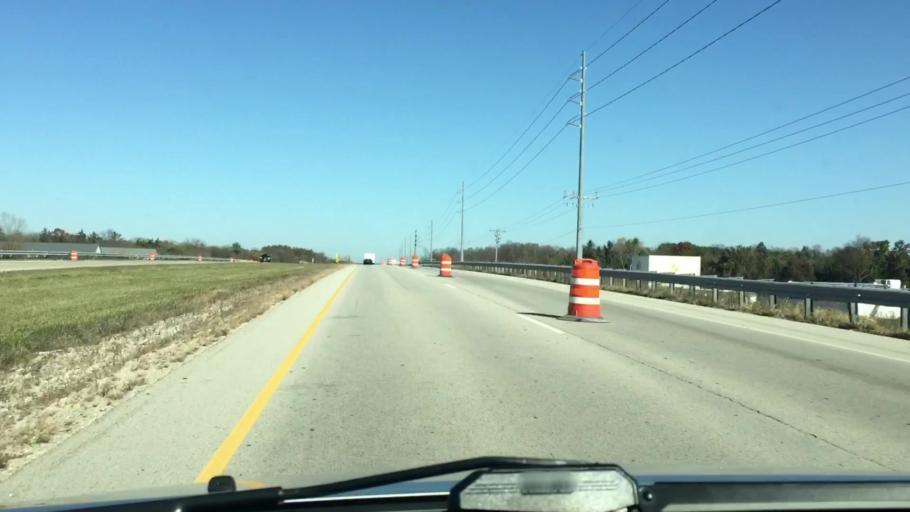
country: US
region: Wisconsin
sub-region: Waukesha County
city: Pewaukee
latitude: 43.0721
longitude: -88.2056
